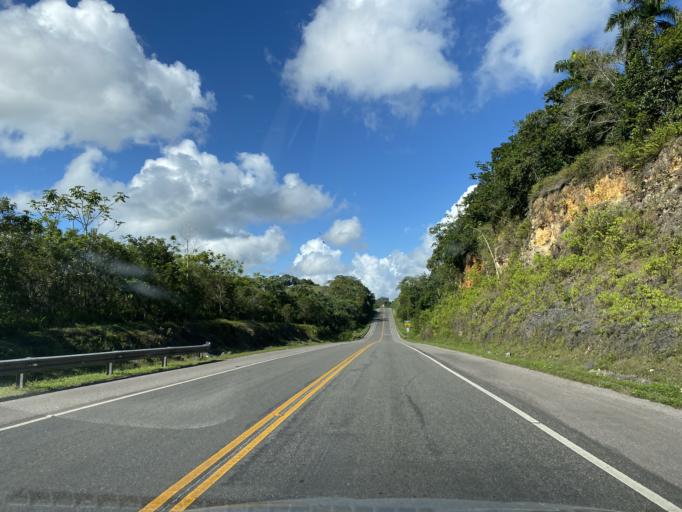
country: DO
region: Monte Plata
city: Majagual
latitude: 19.0334
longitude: -69.8265
